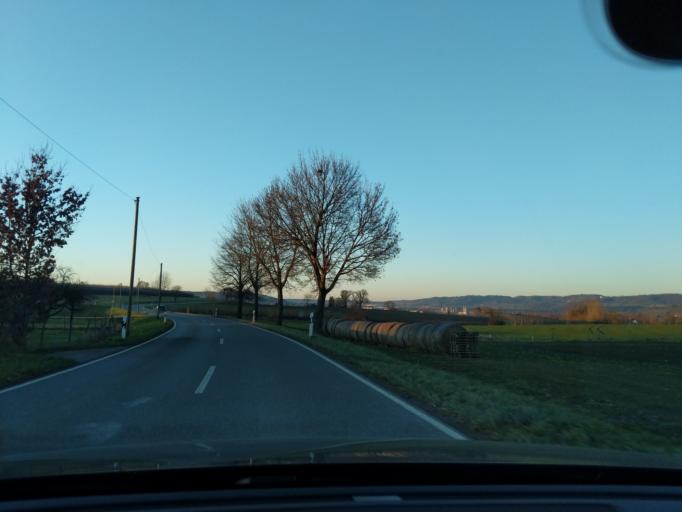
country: DE
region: Baden-Wuerttemberg
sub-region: Tuebingen Region
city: Salem
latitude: 47.7371
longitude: 9.3112
